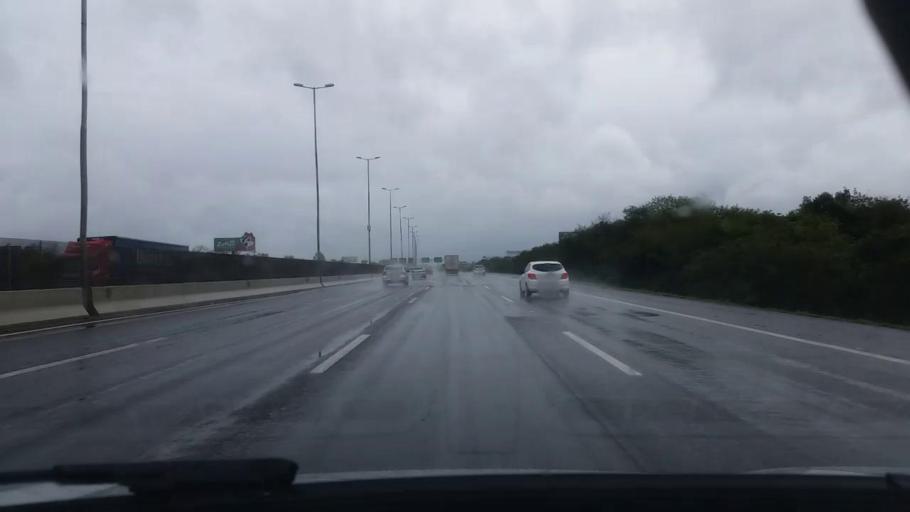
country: BR
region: Rio Grande do Sul
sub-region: Canoas
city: Canoas
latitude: -29.9682
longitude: -51.1592
